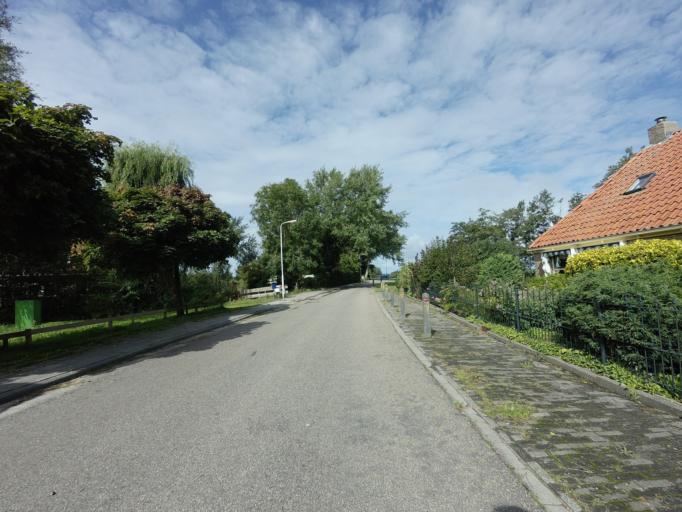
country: NL
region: Friesland
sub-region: Sudwest Fryslan
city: Makkum
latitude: 53.0851
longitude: 5.4233
